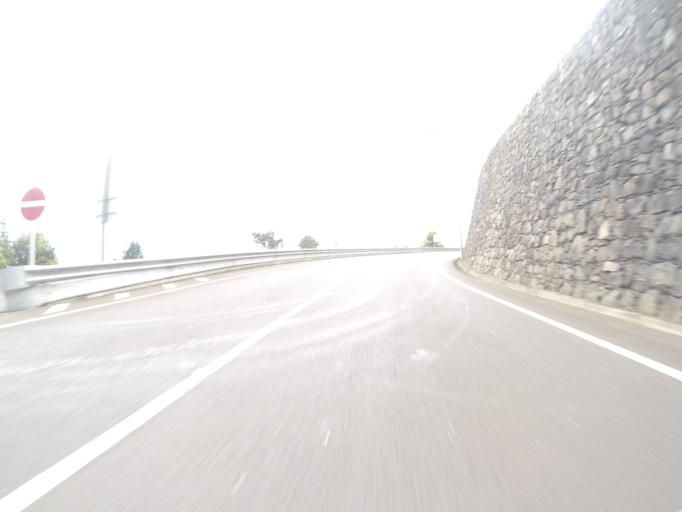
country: PT
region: Madeira
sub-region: Sao Vicente
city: Sao Vicente
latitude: 32.8156
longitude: -17.0975
